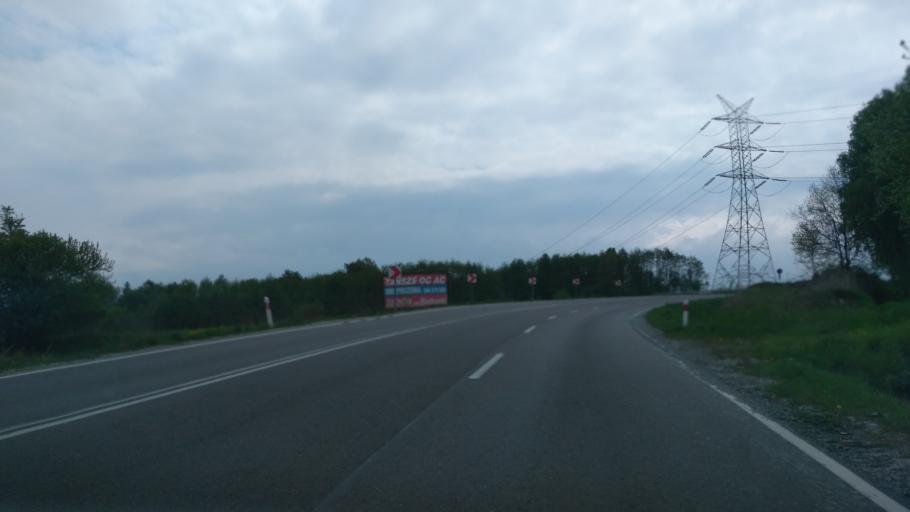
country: PL
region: Lesser Poland Voivodeship
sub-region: Powiat tarnowski
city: Tarnowiec
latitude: 49.9495
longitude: 21.0133
